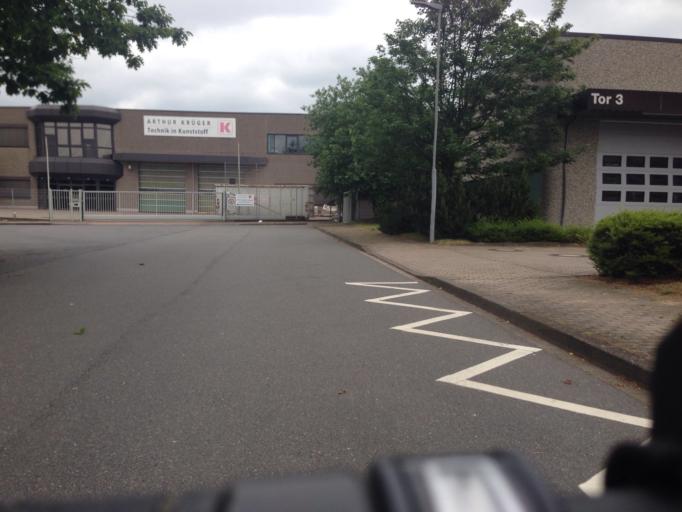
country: DE
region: Schleswig-Holstein
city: Barsbuettel
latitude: 53.5752
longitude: 10.1917
